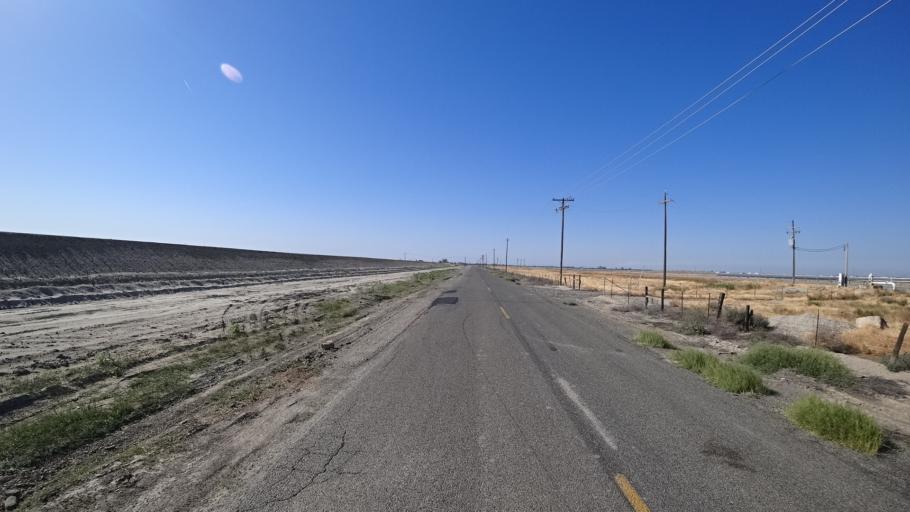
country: US
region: California
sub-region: Kings County
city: Corcoran
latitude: 36.1452
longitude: -119.5649
